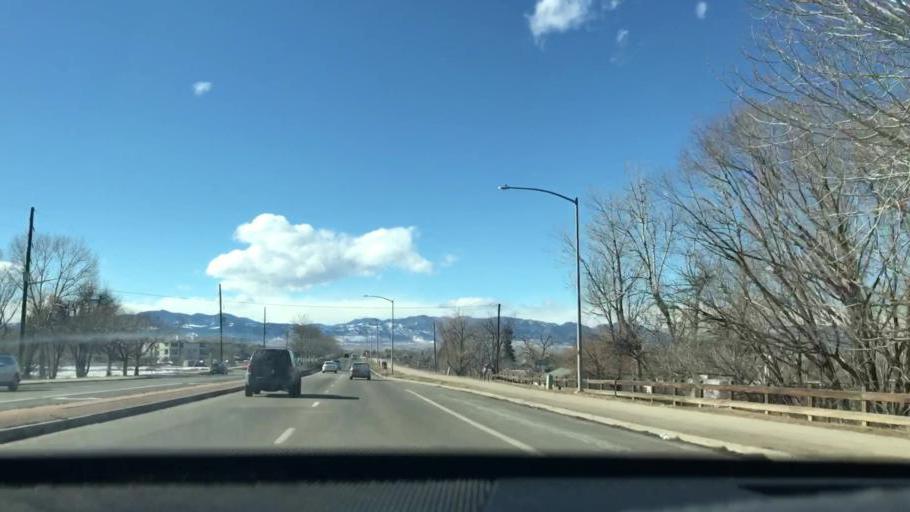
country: US
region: Colorado
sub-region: Adams County
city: Westminster
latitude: 39.8638
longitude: -105.0729
